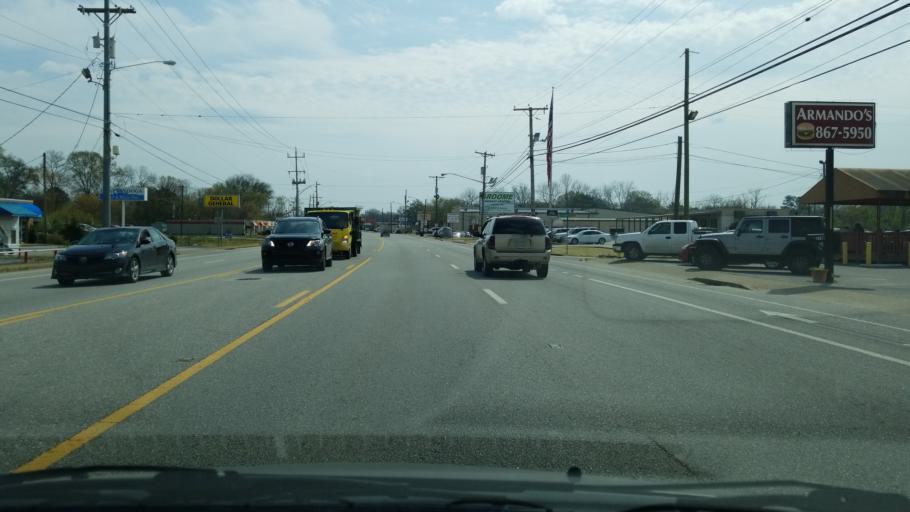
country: US
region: Tennessee
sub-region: Hamilton County
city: East Ridge
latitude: 34.9914
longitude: -85.2247
